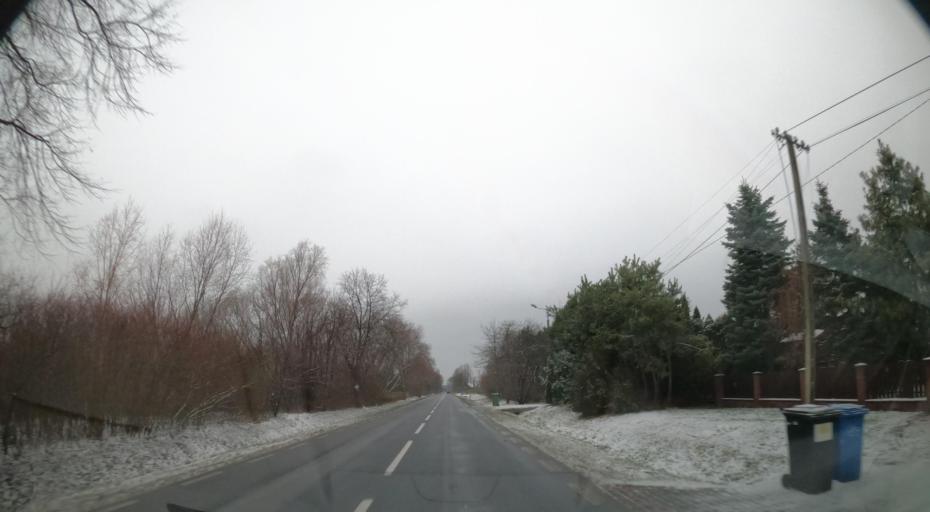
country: PL
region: Masovian Voivodeship
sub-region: Powiat plocki
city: Maszewo Duze
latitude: 52.5717
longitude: 19.5986
